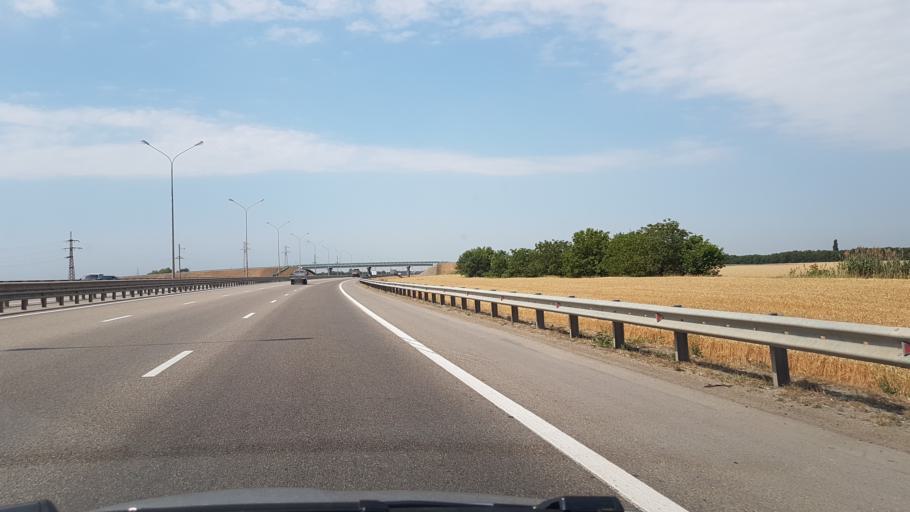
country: RU
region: Krasnodarskiy
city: Dinskaya
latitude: 45.2214
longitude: 39.1779
